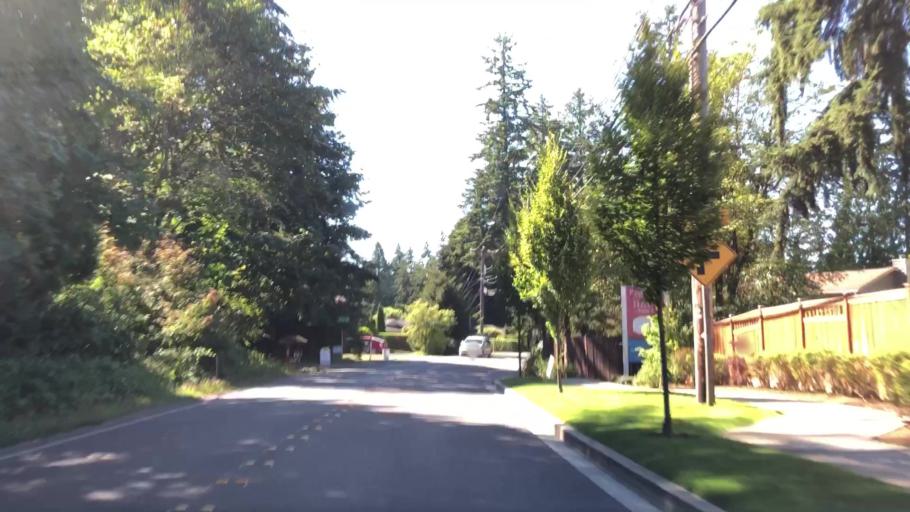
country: US
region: Washington
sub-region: Snohomish County
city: North Creek
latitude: 47.8161
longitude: -122.1847
